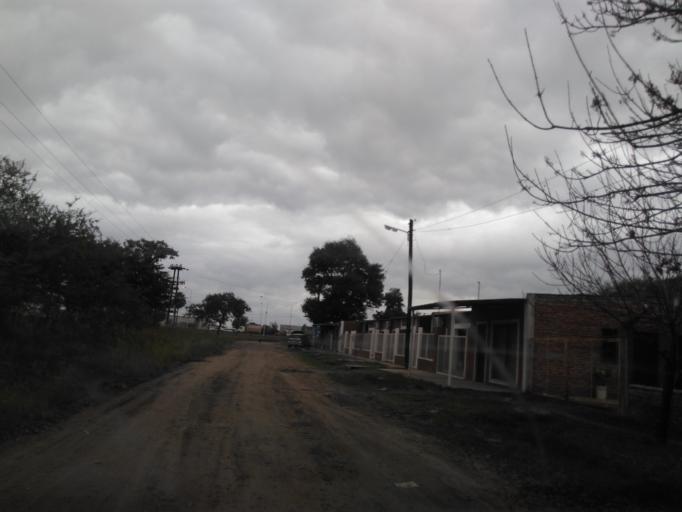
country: AR
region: Chaco
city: Fontana
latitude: -27.4453
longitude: -59.0255
